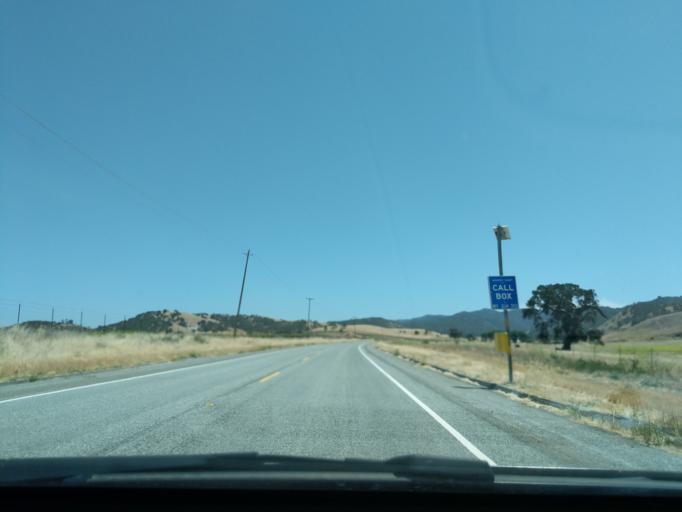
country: US
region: California
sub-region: Monterey County
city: King City
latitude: 36.1492
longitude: -121.1283
